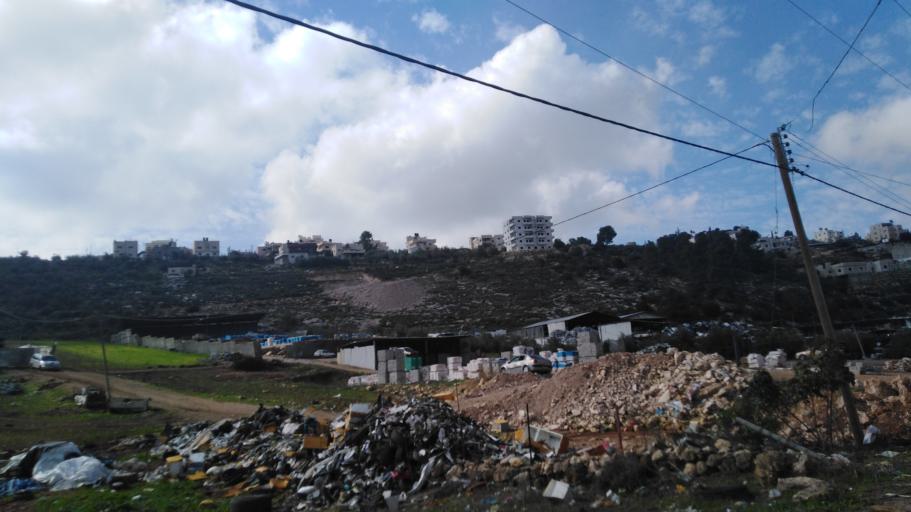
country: PS
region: West Bank
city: Idhna
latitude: 31.5566
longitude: 34.9872
